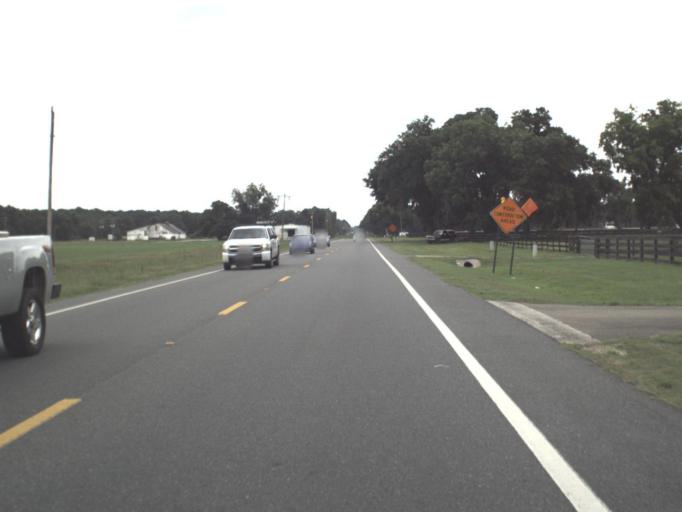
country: US
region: Florida
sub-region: Levy County
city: Williston
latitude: 29.3528
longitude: -82.4558
